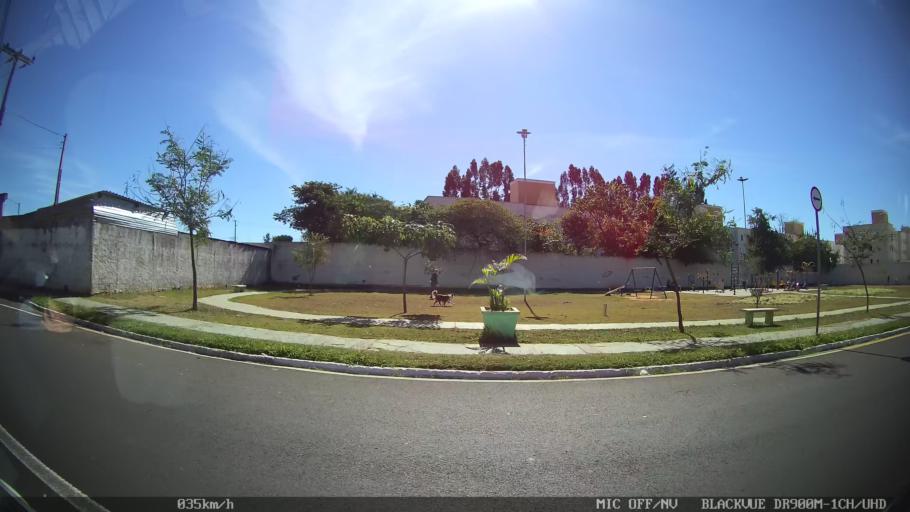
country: BR
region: Sao Paulo
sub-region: Franca
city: Franca
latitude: -20.5419
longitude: -47.3805
